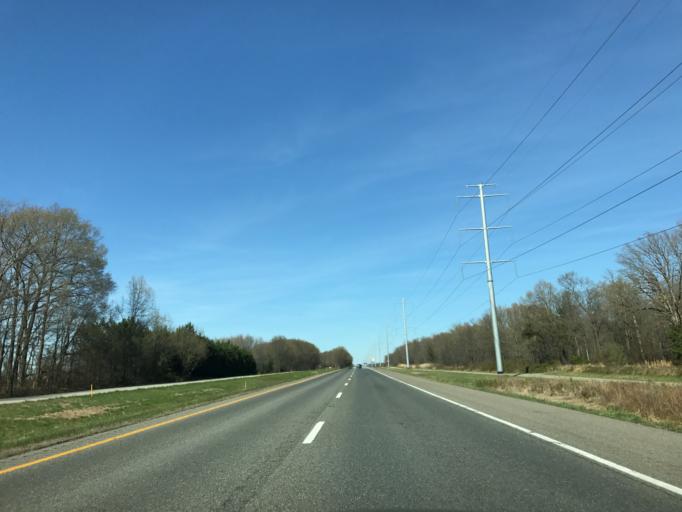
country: US
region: Maryland
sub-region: Queen Anne's County
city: Centreville
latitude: 39.0676
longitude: -75.9883
